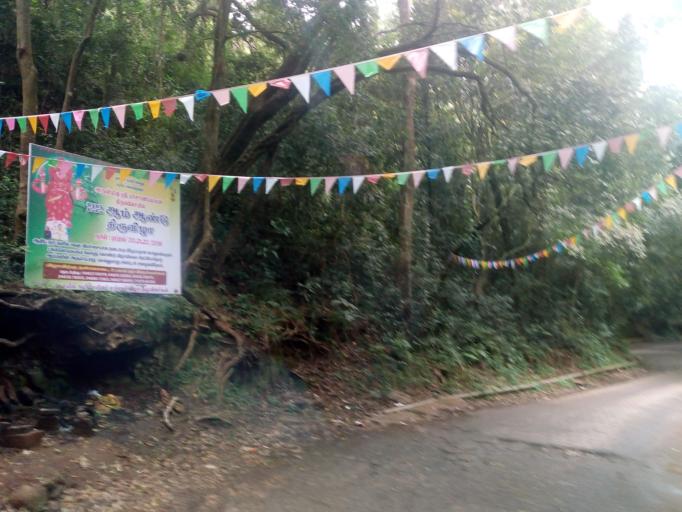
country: IN
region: Tamil Nadu
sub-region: Nilgiri
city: Wellington
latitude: 11.3495
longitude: 76.8167
